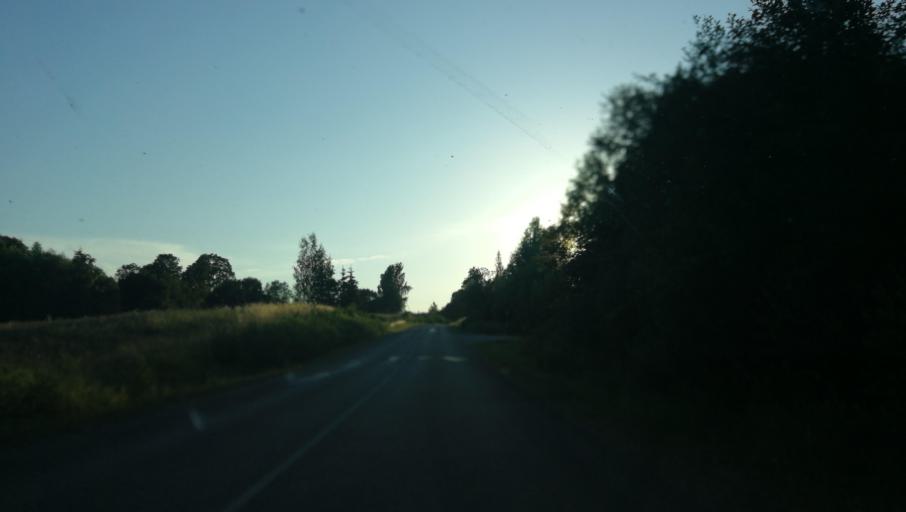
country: LV
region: Priekuli
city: Priekuli
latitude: 57.2593
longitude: 25.3652
